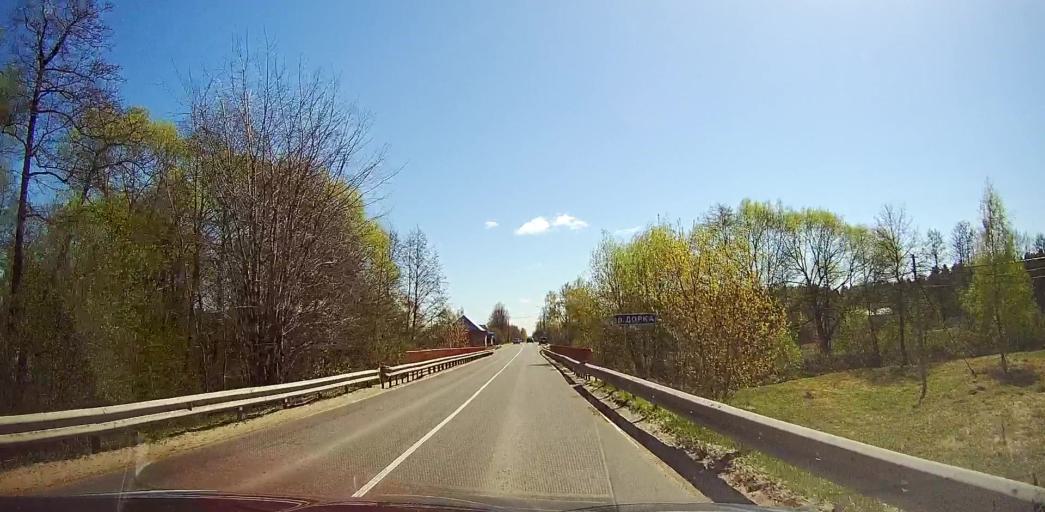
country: RU
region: Moskovskaya
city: Rechitsy
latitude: 55.5390
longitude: 38.4229
